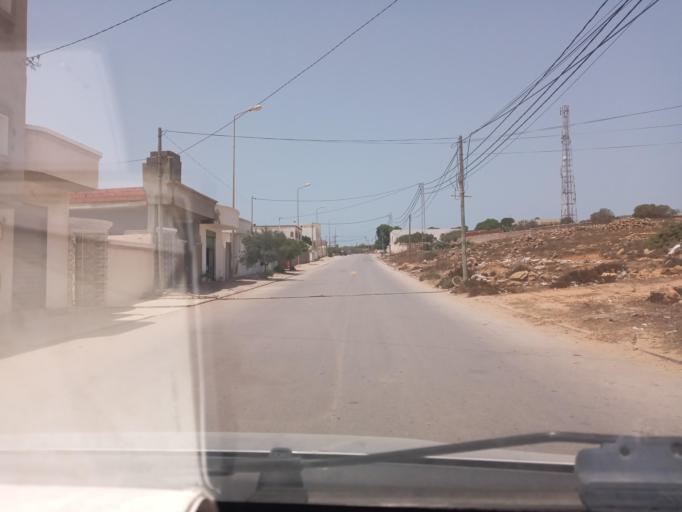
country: TN
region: Nabul
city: El Haouaria
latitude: 37.0547
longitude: 11.0046
